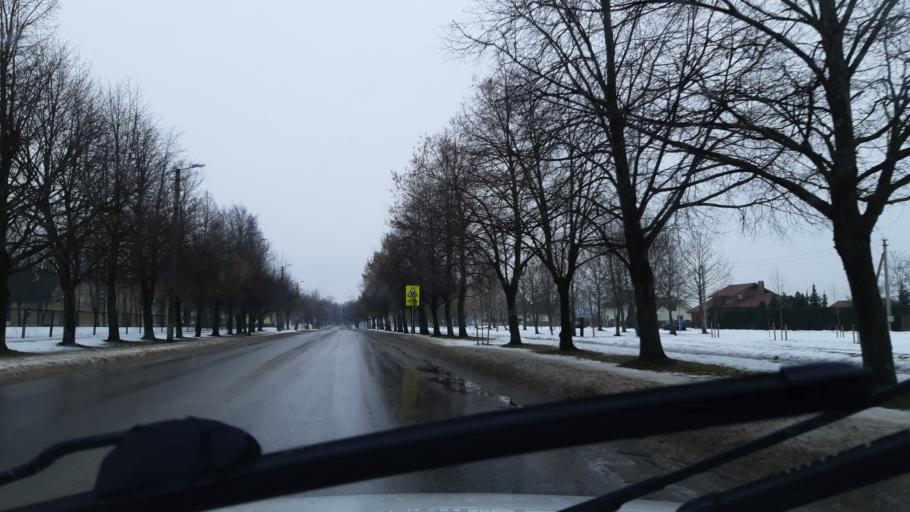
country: LT
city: Vilkaviskis
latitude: 54.6547
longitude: 23.0277
